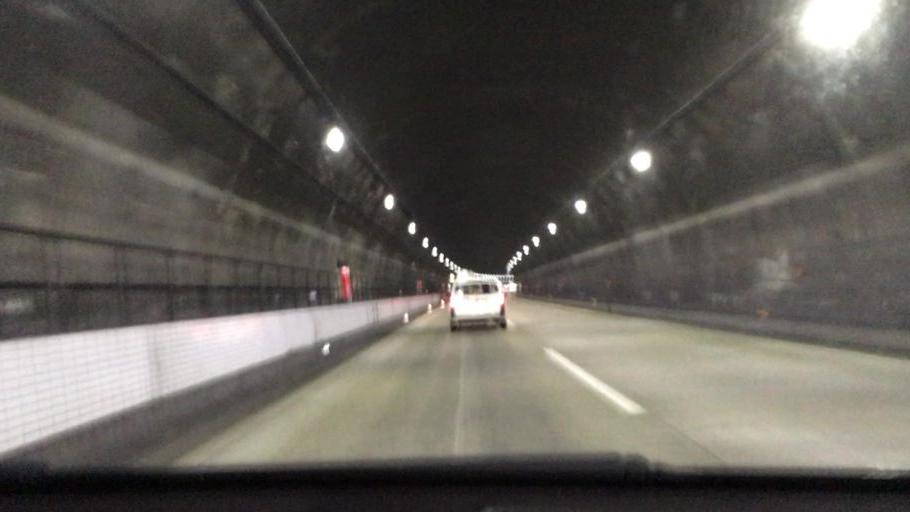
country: JP
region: Yamaguchi
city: Tokuyama
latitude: 34.0711
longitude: 131.7096
